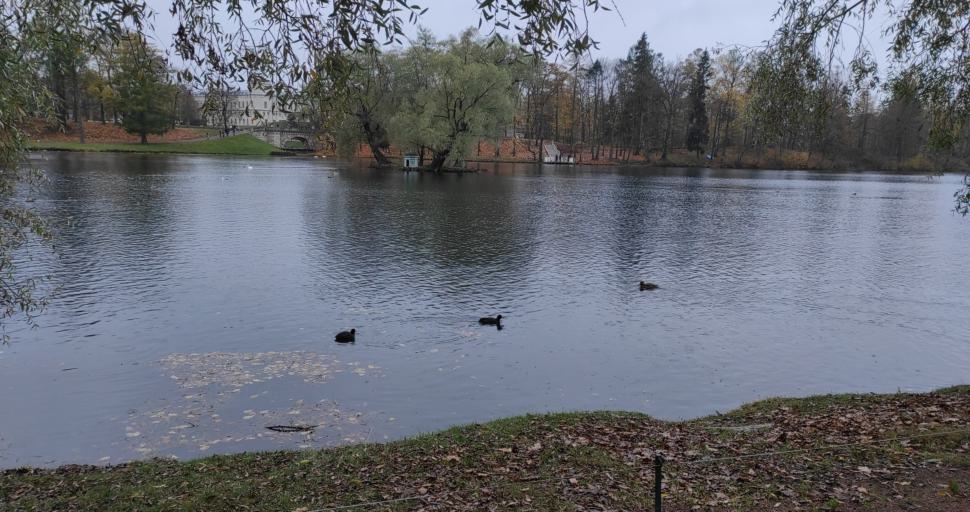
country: RU
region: Leningrad
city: Gatchina
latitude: 59.5642
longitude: 30.1153
